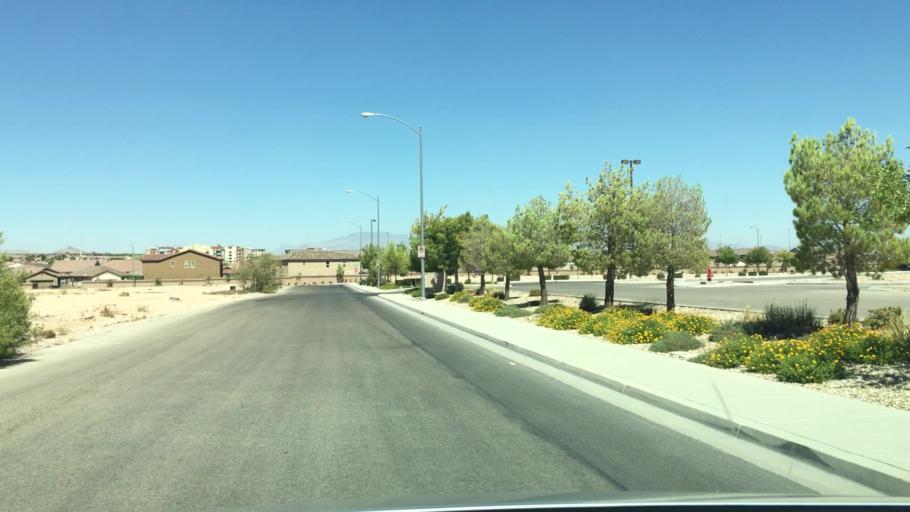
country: US
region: Nevada
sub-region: Clark County
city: Summerlin South
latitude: 36.0742
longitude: -115.2931
